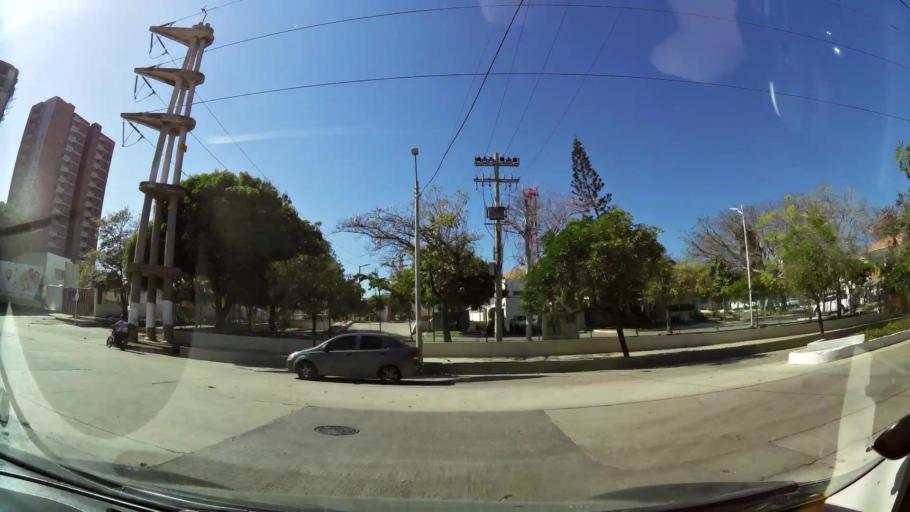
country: CO
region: Atlantico
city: Barranquilla
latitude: 11.0025
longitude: -74.7898
